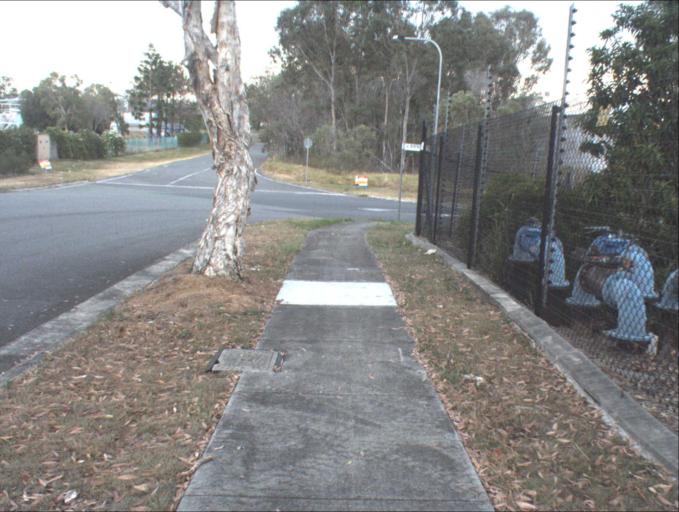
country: AU
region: Queensland
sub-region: Logan
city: Beenleigh
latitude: -27.6839
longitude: 153.1938
